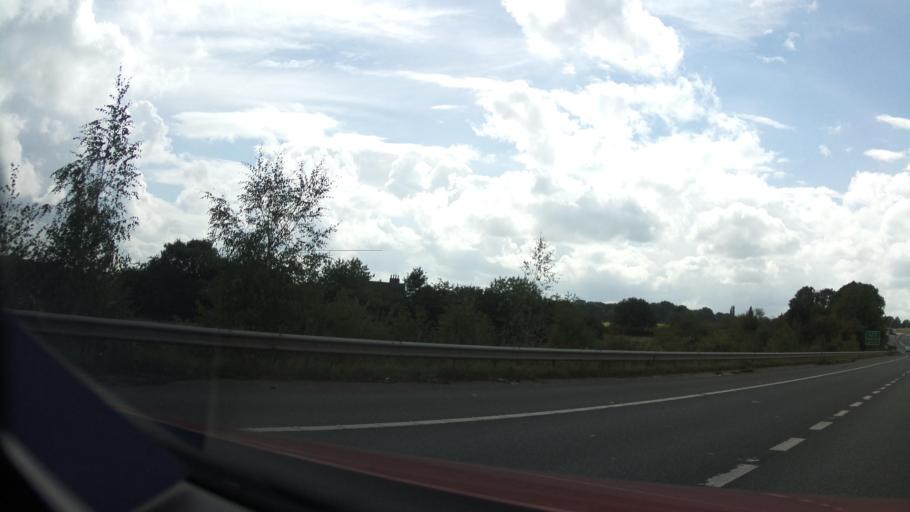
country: GB
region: England
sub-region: Trafford
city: Bowdon
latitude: 53.3627
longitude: -2.3926
